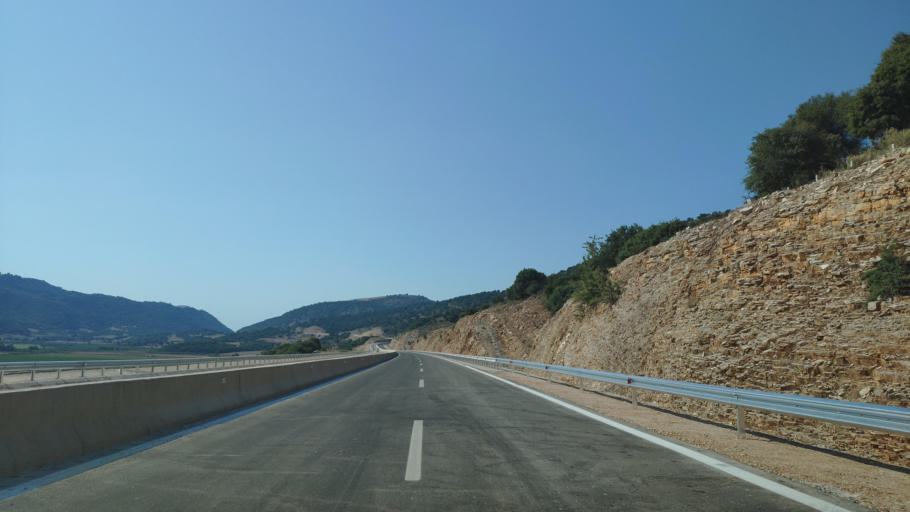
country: GR
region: West Greece
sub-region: Nomos Aitolias kai Akarnanias
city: Katouna
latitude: 38.8260
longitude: 21.1227
